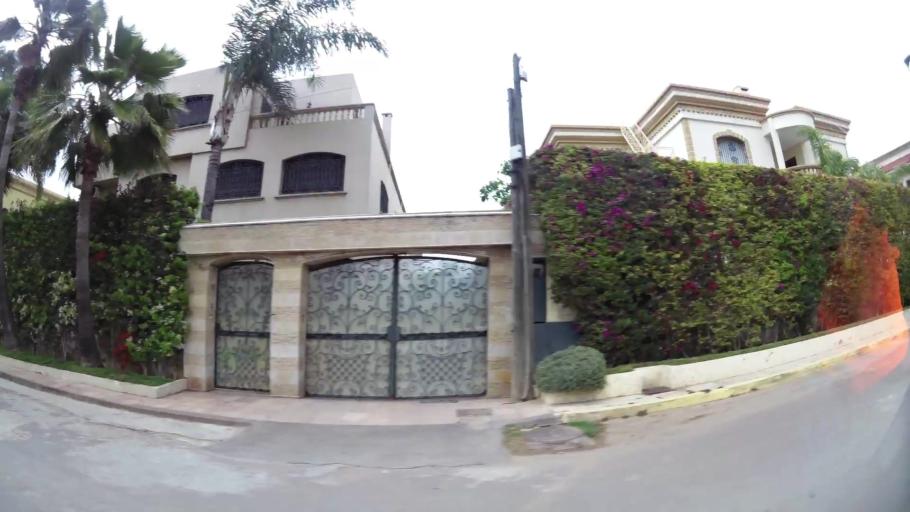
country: MA
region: Grand Casablanca
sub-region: Casablanca
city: Casablanca
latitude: 33.5453
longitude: -7.6404
